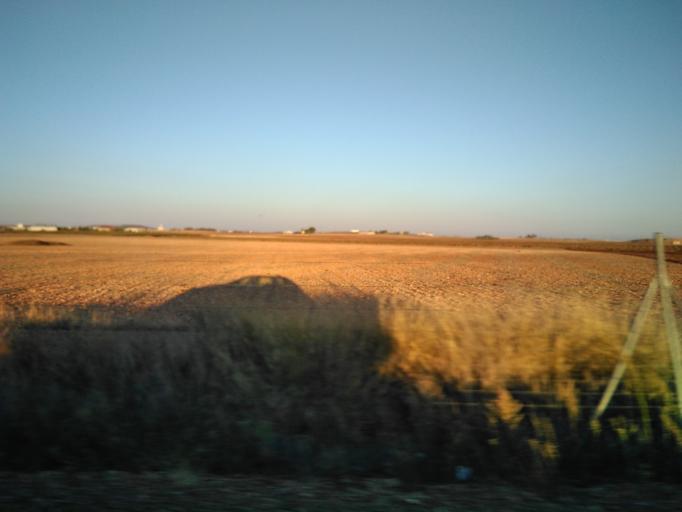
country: ES
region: Castille-La Mancha
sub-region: Provincia de Ciudad Real
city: Miguelturra
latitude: 38.9523
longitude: -3.9182
